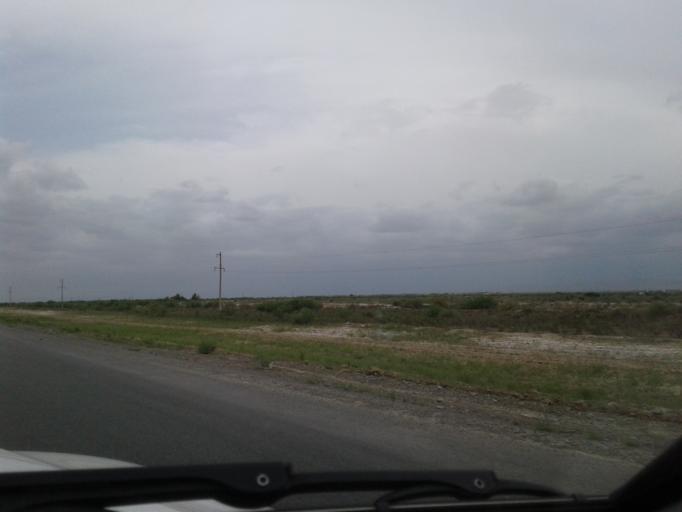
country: TM
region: Ahal
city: Kaka
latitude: 37.4994
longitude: 59.4563
